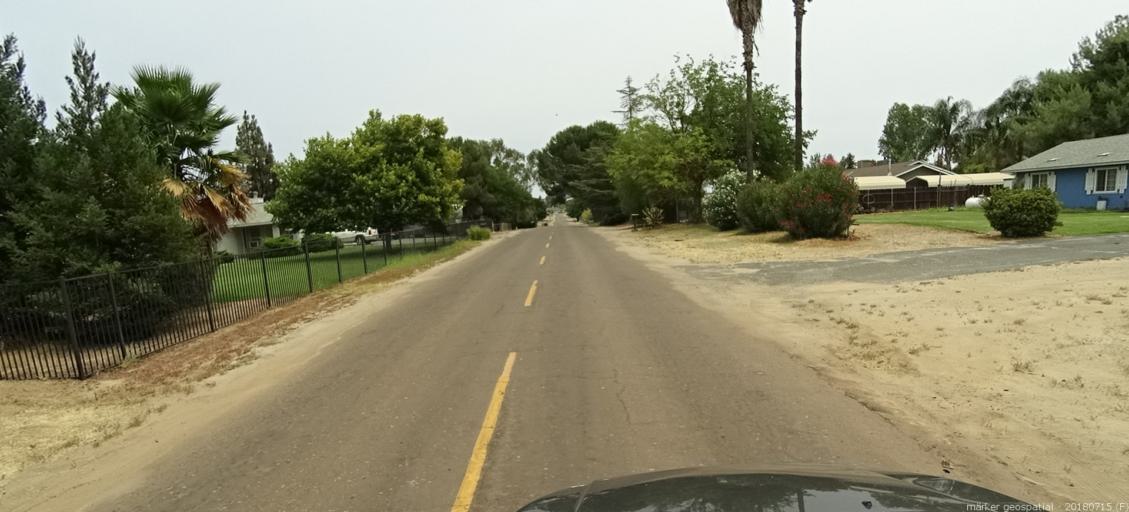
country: US
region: California
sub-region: Madera County
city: Madera Acres
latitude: 37.0064
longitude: -120.0830
